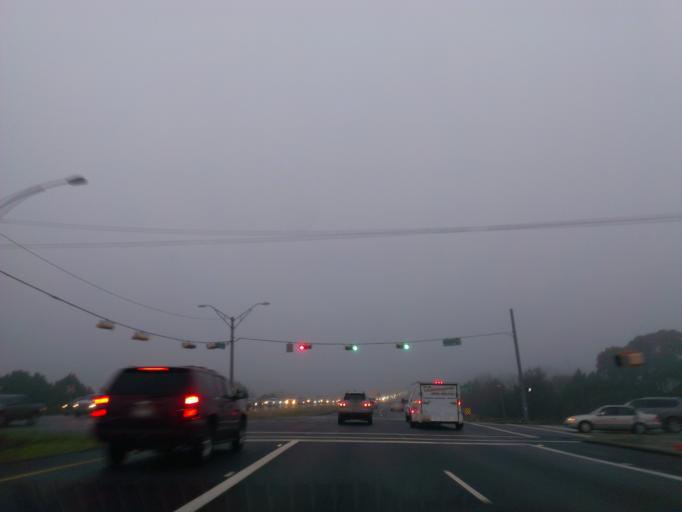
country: US
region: Texas
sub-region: Williamson County
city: Jollyville
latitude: 30.3854
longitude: -97.7663
